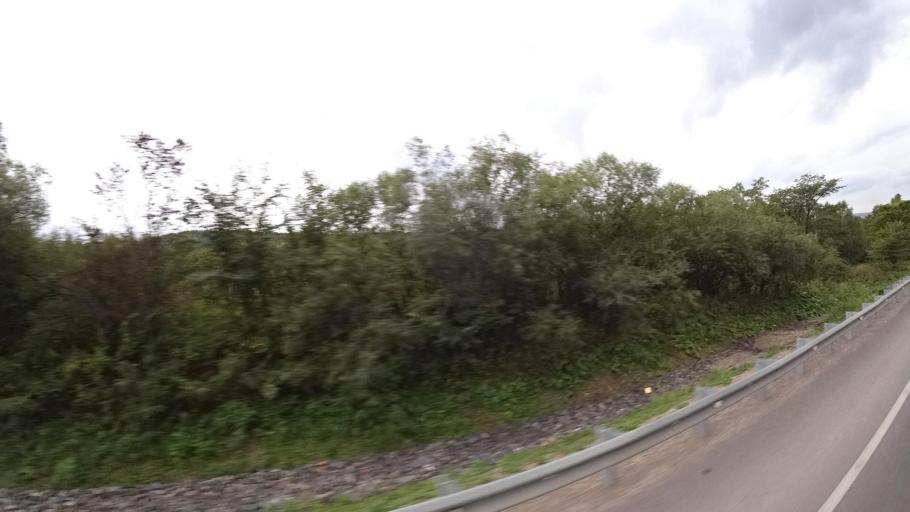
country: RU
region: Jewish Autonomous Oblast
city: Khingansk
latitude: 48.9883
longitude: 131.1311
